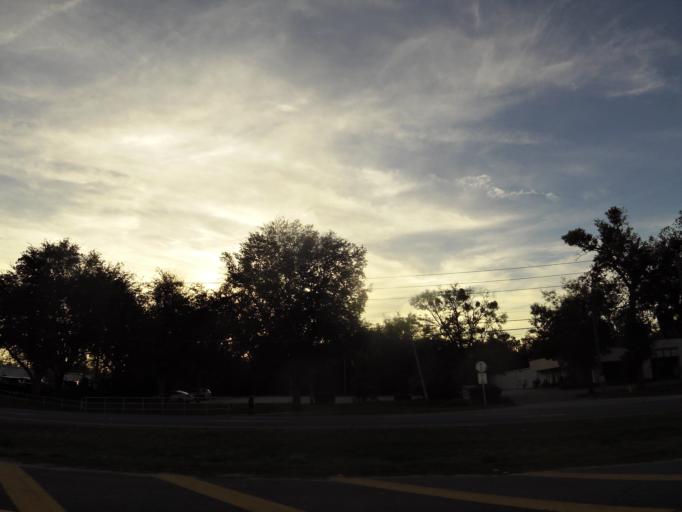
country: US
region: Florida
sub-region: Volusia County
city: De Land Southwest
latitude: 29.0001
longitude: -81.3026
